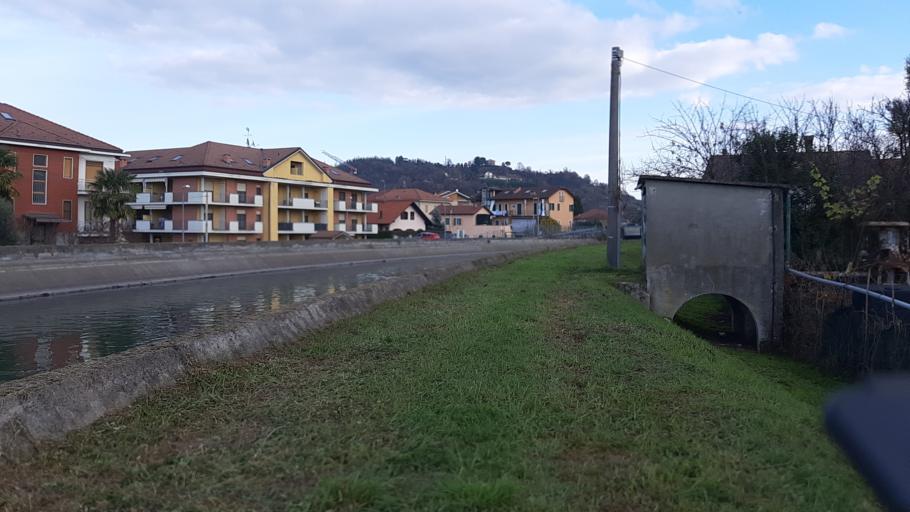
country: IT
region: Piedmont
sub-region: Provincia di Torino
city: Gassino Torinese
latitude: 45.1317
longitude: 7.8245
